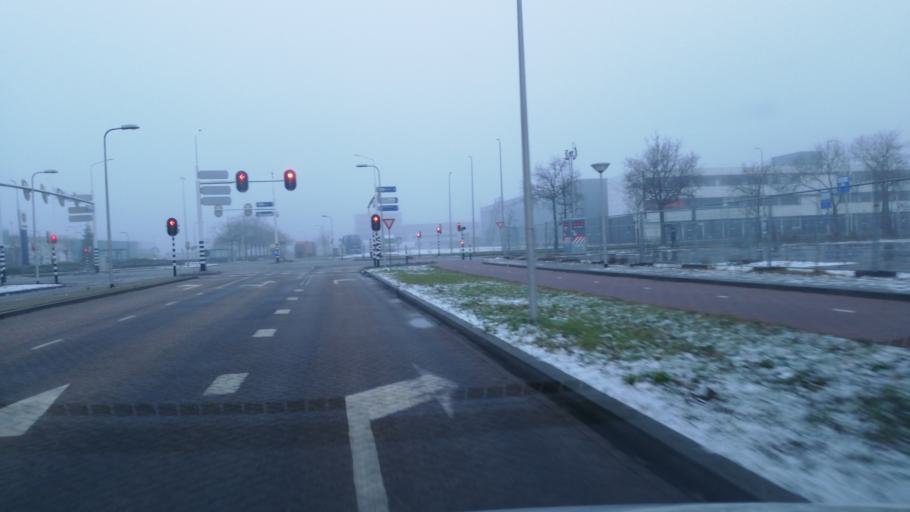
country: NL
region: Overijssel
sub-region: Gemeente Zwolle
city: Zwolle
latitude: 52.5126
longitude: 6.0689
